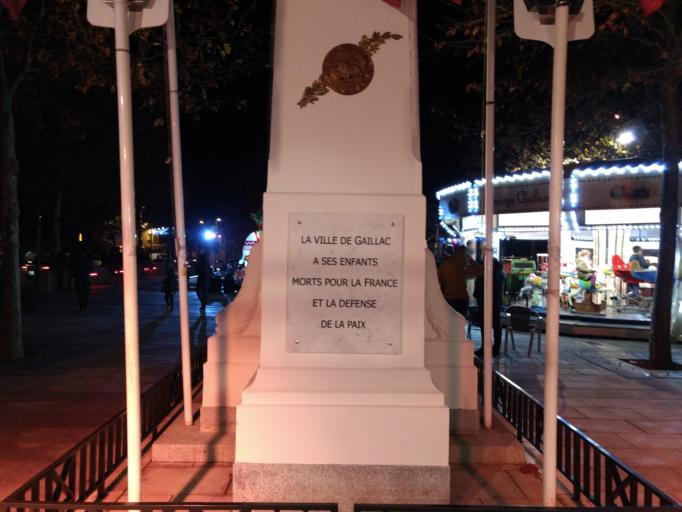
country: FR
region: Midi-Pyrenees
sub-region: Departement du Tarn
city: Gaillac
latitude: 43.8999
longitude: 1.8980
